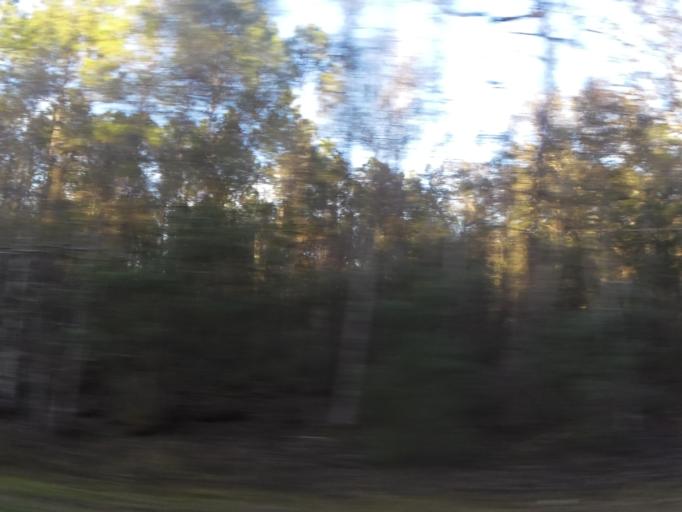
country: US
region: Florida
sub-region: Putnam County
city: East Palatka
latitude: 29.7959
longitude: -81.5199
